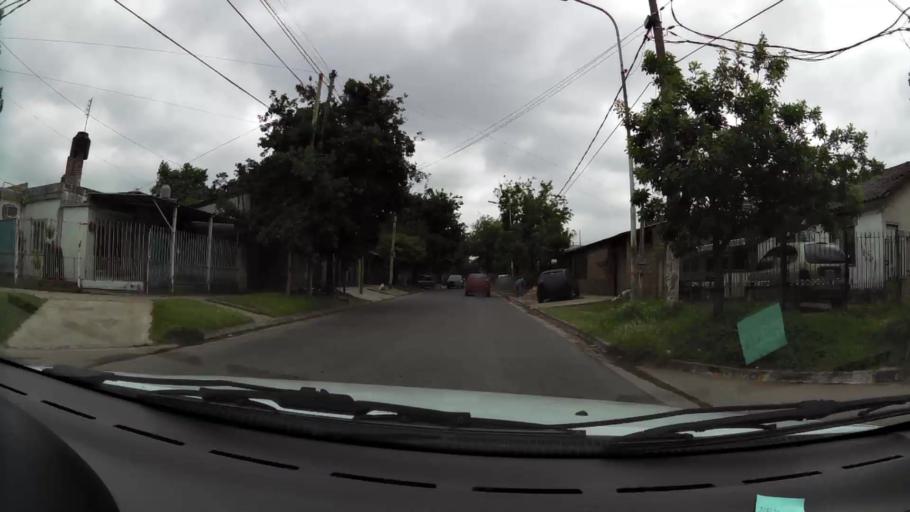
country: AR
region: Buenos Aires
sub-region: Partido de Ezeiza
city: Ezeiza
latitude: -34.8447
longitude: -58.5136
